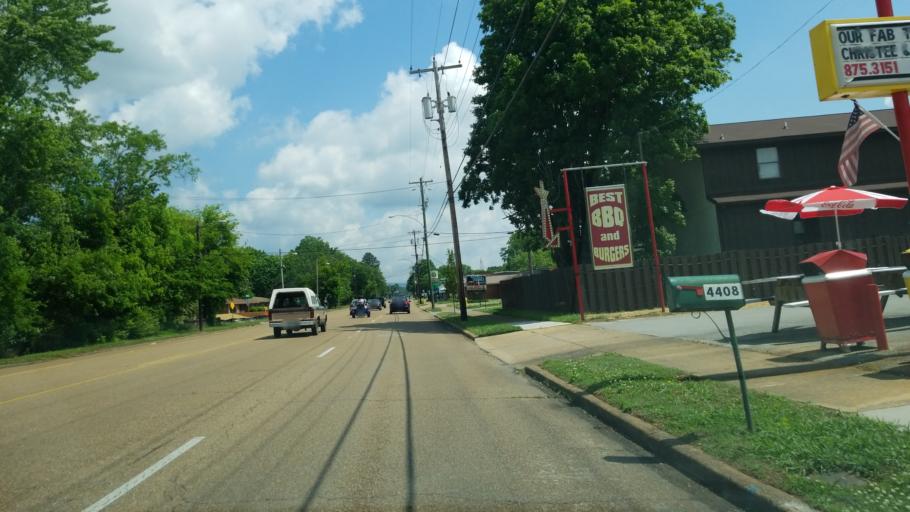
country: US
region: Tennessee
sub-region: Hamilton County
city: Red Bank
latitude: 35.1273
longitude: -85.2843
